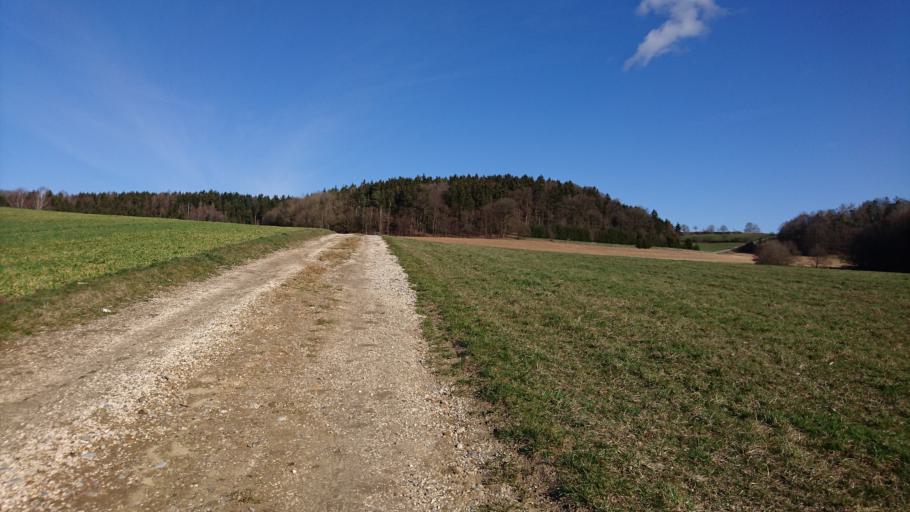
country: DE
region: Bavaria
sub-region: Swabia
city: Altenmunster
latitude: 48.4495
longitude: 10.6025
